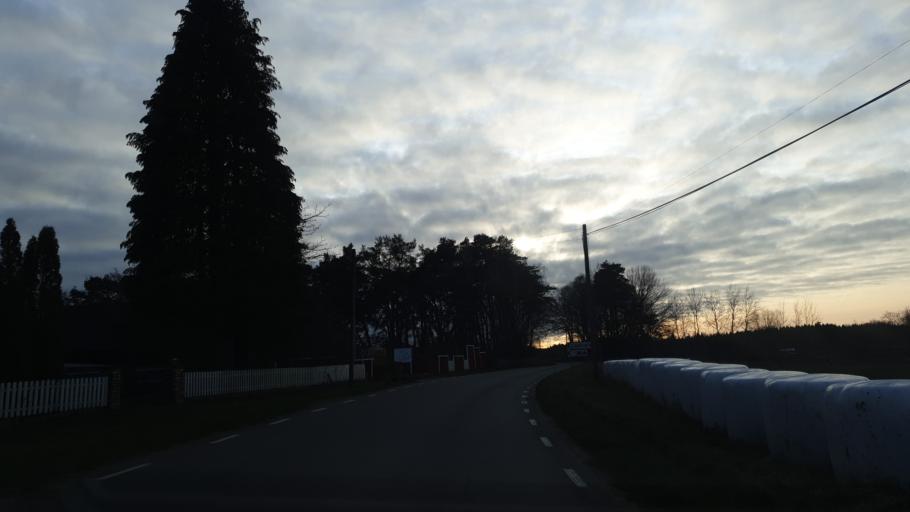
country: SE
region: Blekinge
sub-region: Karlskrona Kommun
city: Jaemjoe
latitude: 56.1876
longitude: 15.9443
